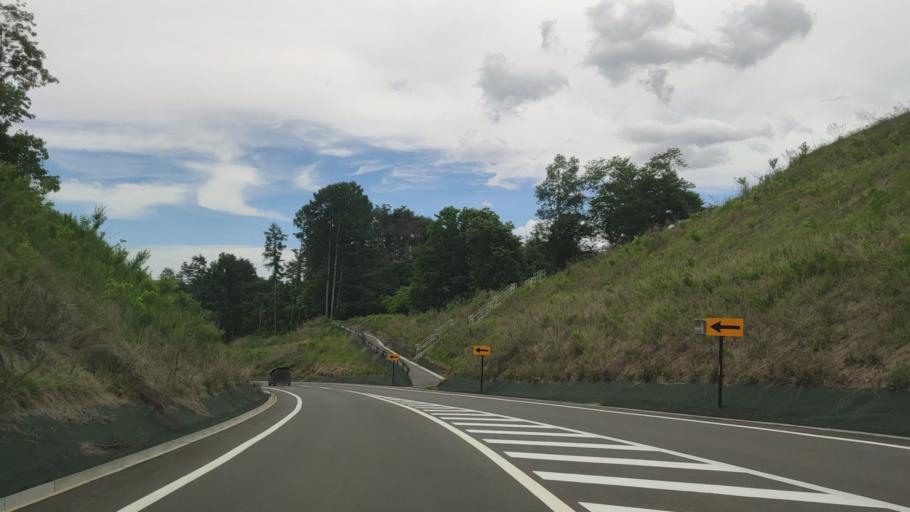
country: JP
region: Nagano
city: Kamimaruko
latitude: 36.2768
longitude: 138.2937
